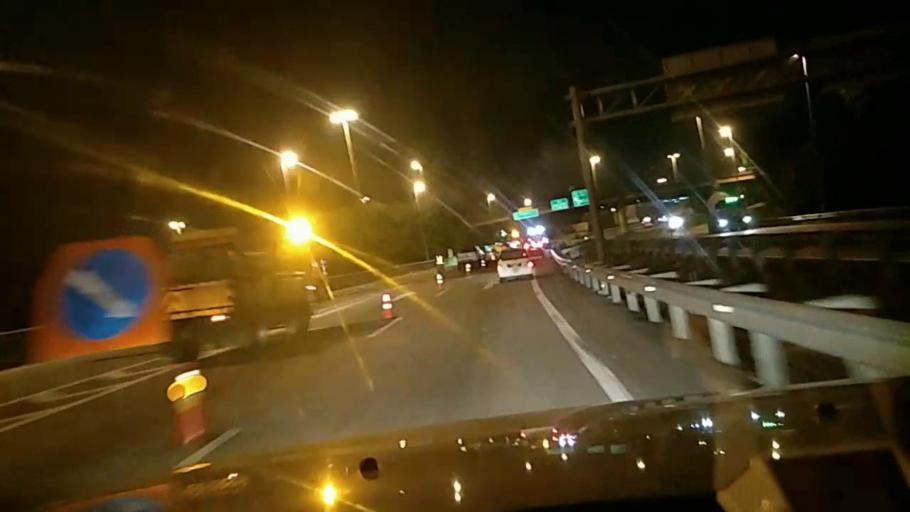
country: MY
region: Penang
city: Perai
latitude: 5.3630
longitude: 100.4010
